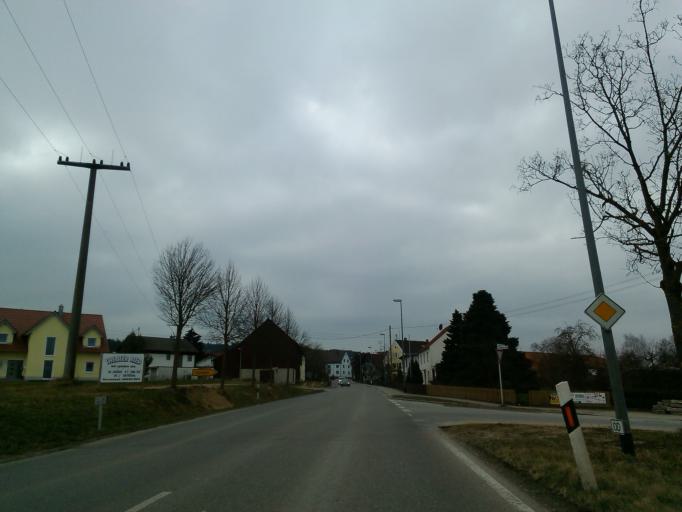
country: DE
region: Bavaria
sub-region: Swabia
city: Ustersbach
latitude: 48.3087
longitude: 10.6161
